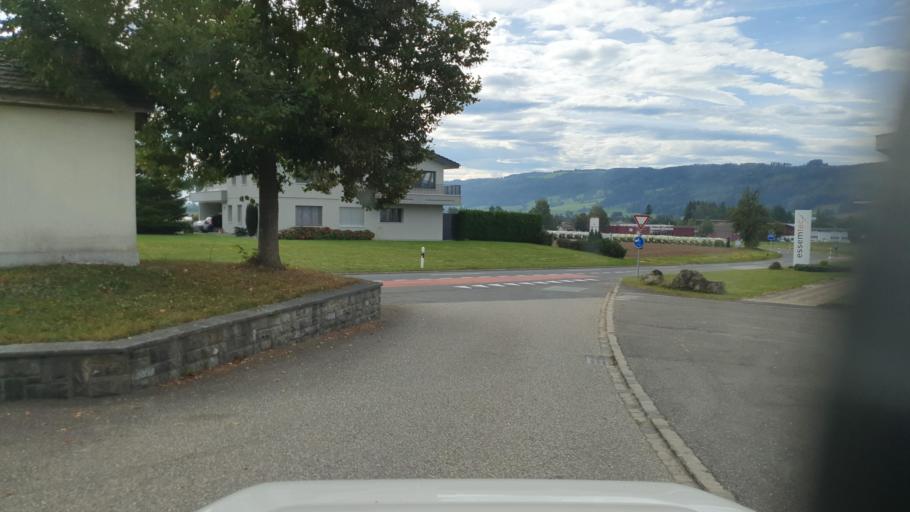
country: CH
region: Lucerne
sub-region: Hochdorf District
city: Hitzkirch
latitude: 47.2519
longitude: 8.2386
